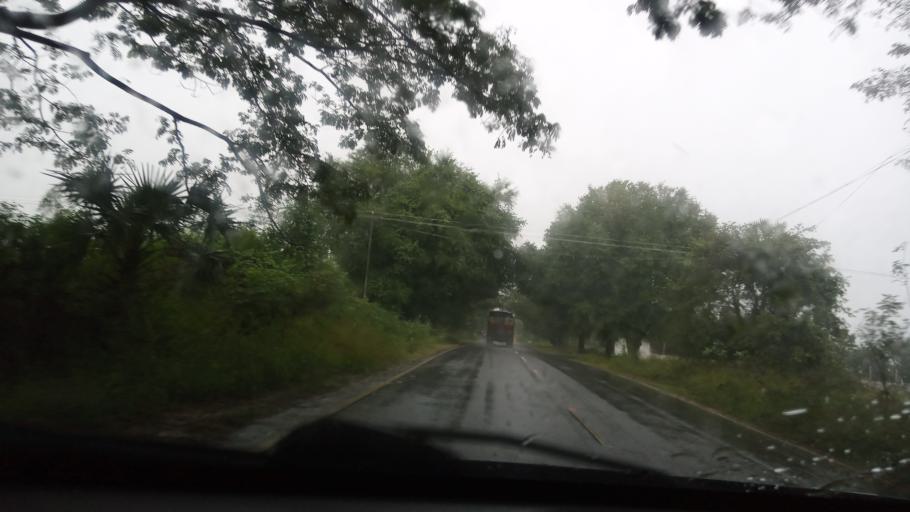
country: IN
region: Tamil Nadu
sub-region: Vellore
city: Kalavai
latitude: 12.8156
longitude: 79.4117
